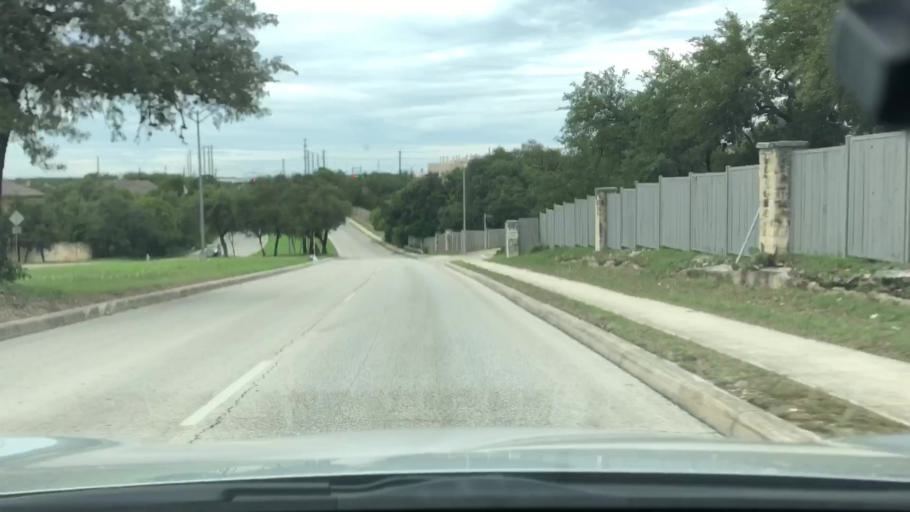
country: US
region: Texas
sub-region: Bexar County
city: Leon Valley
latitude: 29.4654
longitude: -98.6743
